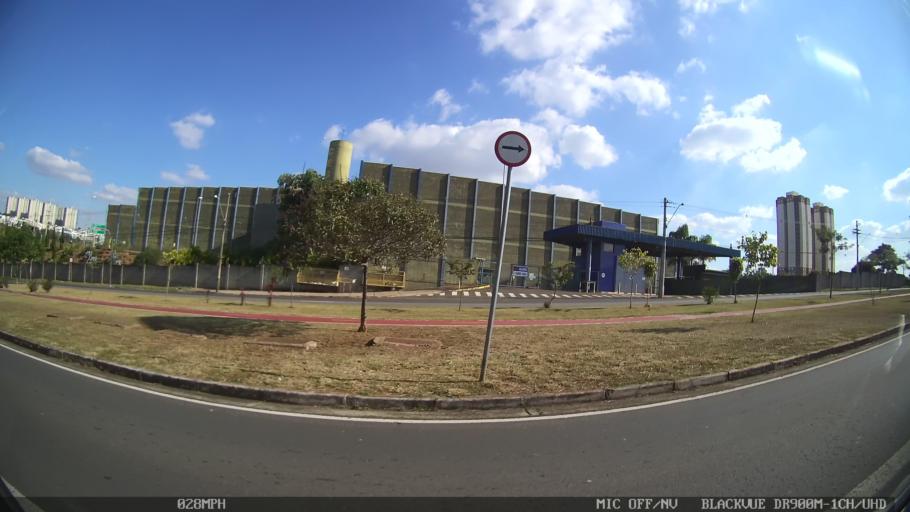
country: BR
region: Sao Paulo
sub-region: Nova Odessa
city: Nova Odessa
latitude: -22.7784
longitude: -47.3067
